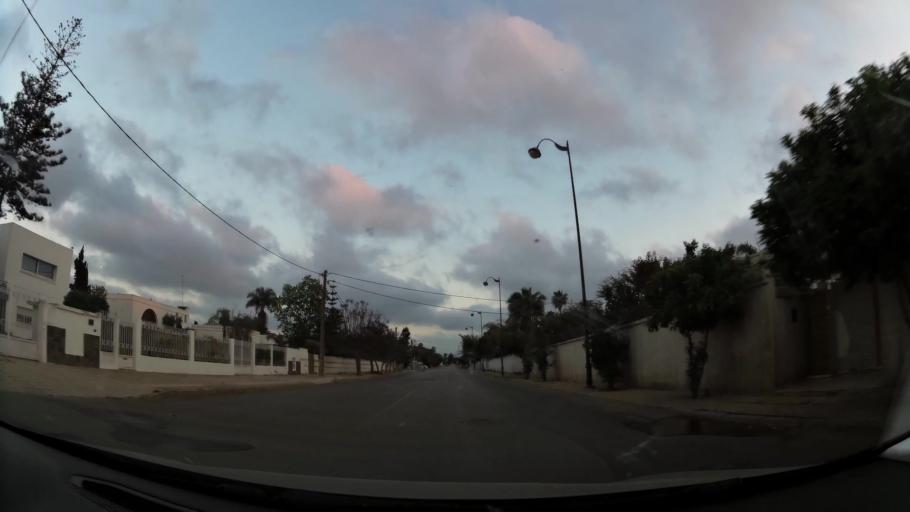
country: MA
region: Rabat-Sale-Zemmour-Zaer
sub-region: Rabat
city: Rabat
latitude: 33.9651
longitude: -6.8375
